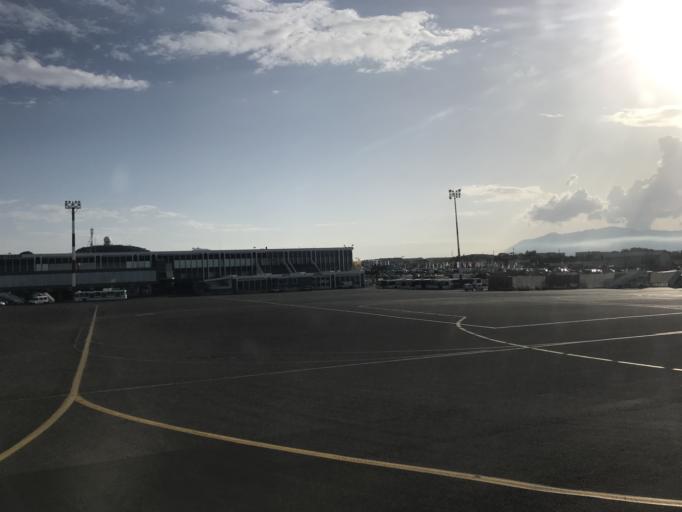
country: GR
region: Crete
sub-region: Nomos Irakleiou
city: Nea Alikarnassos
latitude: 35.3391
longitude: 25.1737
